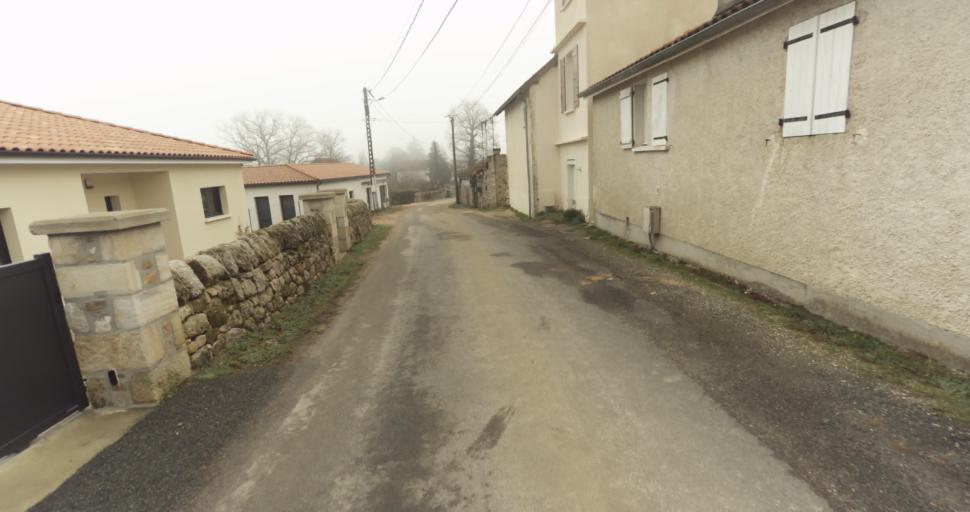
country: FR
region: Midi-Pyrenees
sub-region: Departement du Lot
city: Figeac
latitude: 44.6202
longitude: 2.0392
